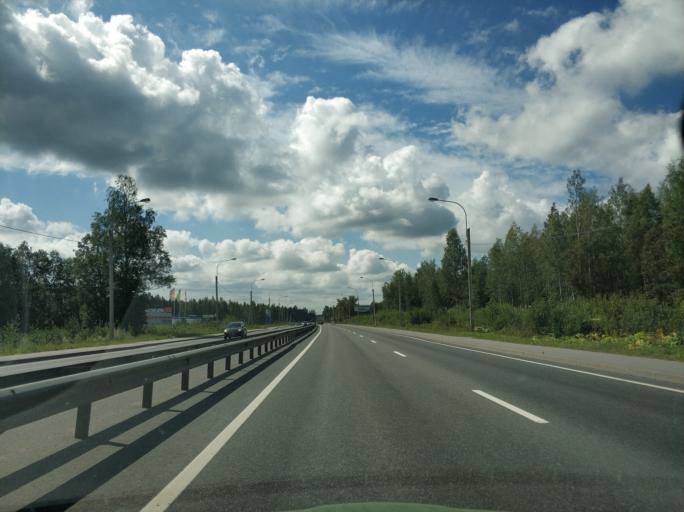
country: RU
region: Leningrad
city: Vsevolozhsk
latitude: 60.0176
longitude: 30.5940
